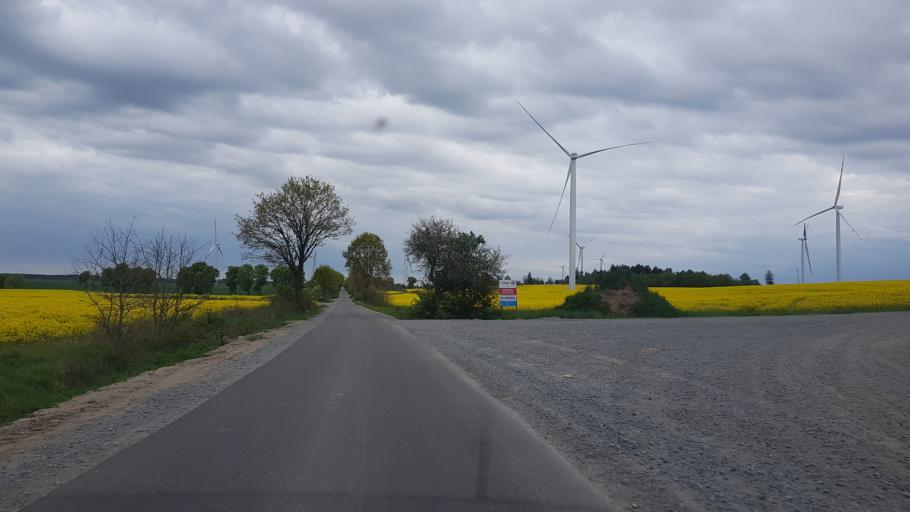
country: PL
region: West Pomeranian Voivodeship
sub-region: Powiat slawienski
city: Slawno
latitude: 54.2590
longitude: 16.5507
